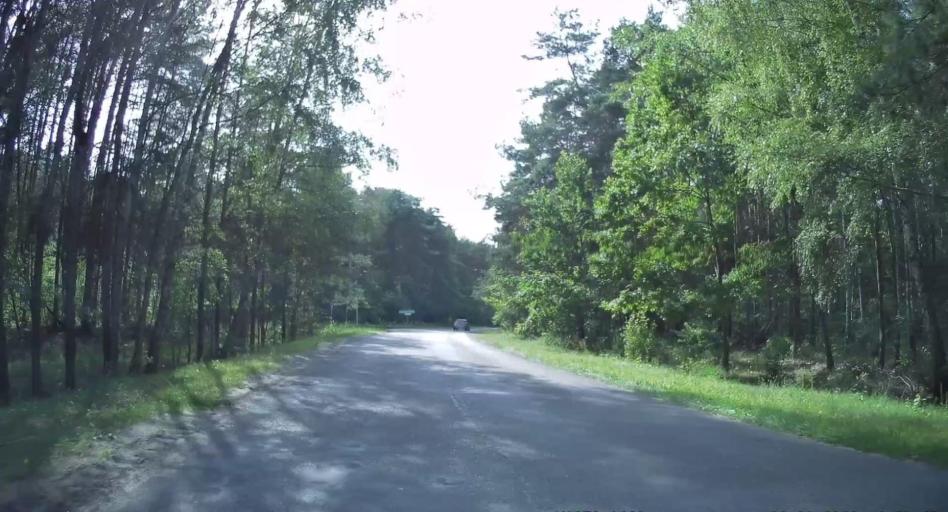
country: DE
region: Thuringia
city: Rohrberg
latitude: 51.4743
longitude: 9.9906
